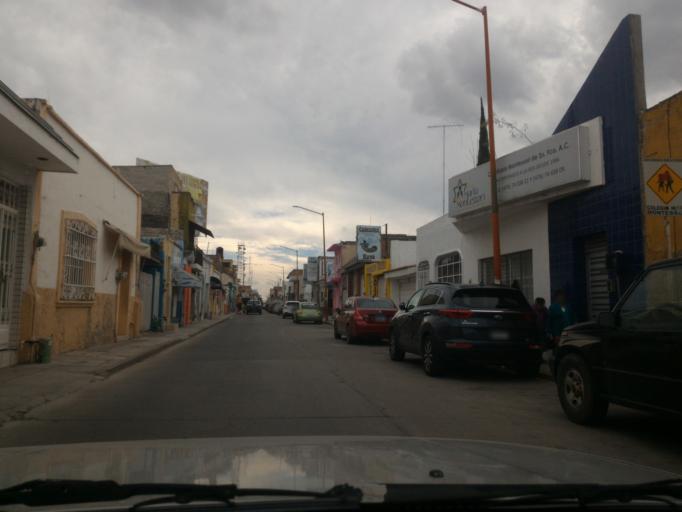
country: MX
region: Guanajuato
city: San Francisco del Rincon
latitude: 21.0223
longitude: -101.8603
